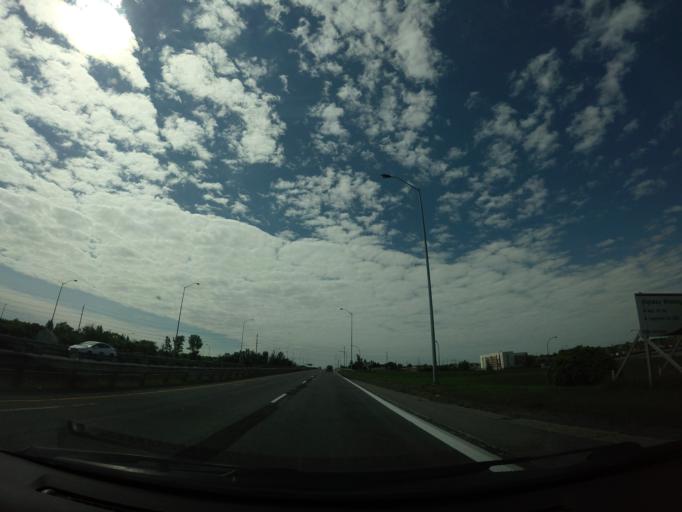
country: CA
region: Quebec
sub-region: Outaouais
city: Gatineau
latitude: 45.4527
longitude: -75.5829
